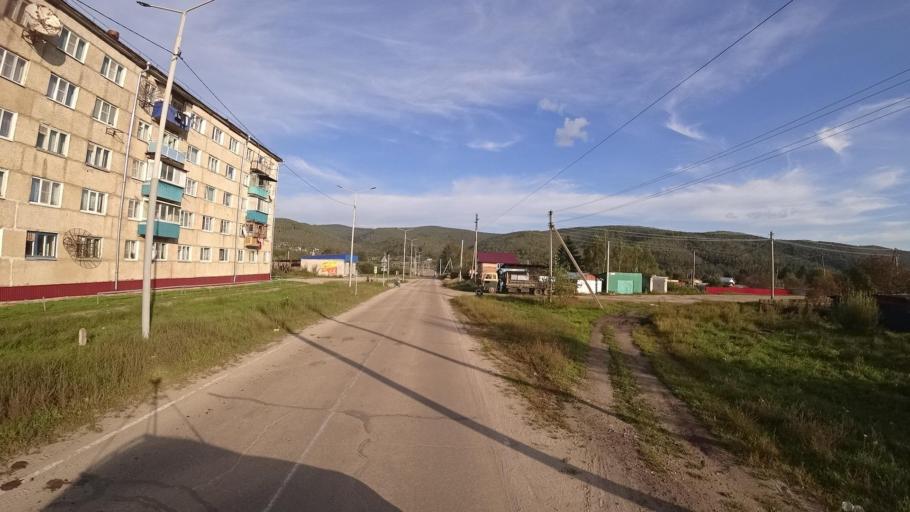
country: RU
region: Jewish Autonomous Oblast
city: Kul'dur
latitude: 49.2013
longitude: 131.6262
